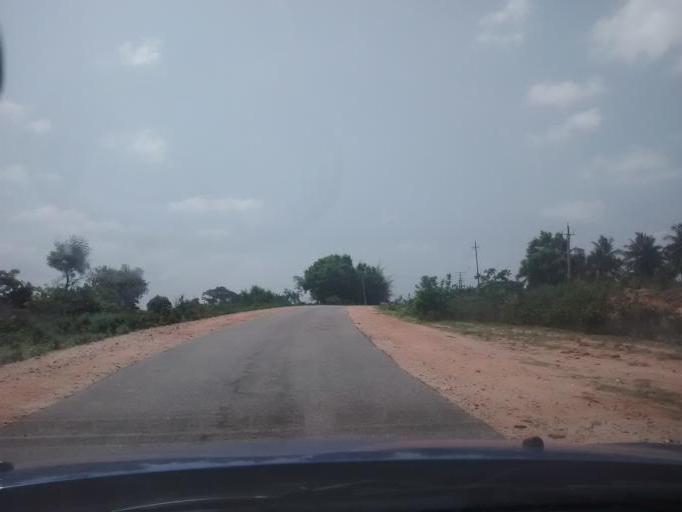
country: IN
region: Karnataka
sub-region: Hassan
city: Konanur
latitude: 12.5664
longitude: 76.2409
